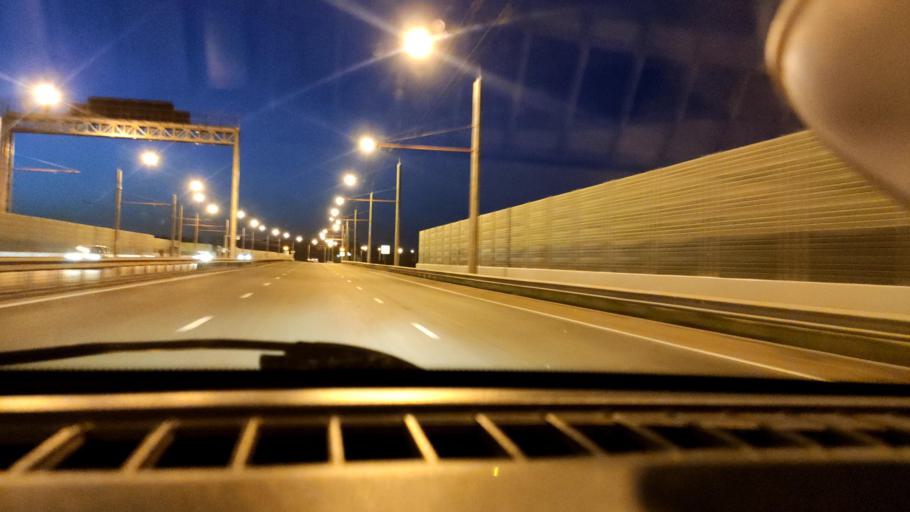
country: RU
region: Samara
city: Samara
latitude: 53.1620
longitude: 50.0877
